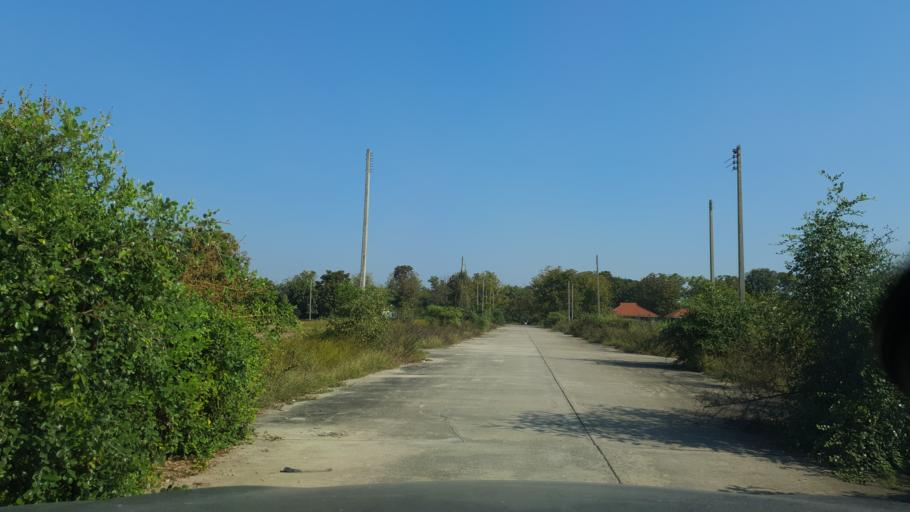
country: TH
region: Lamphun
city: Ban Thi
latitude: 18.6762
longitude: 99.1228
